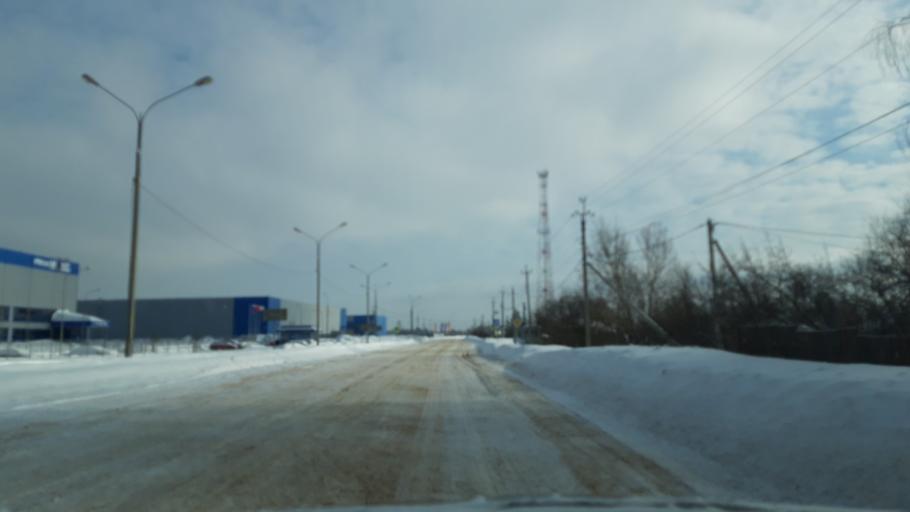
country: RU
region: Moskovskaya
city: Yermolino
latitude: 56.1441
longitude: 37.3751
